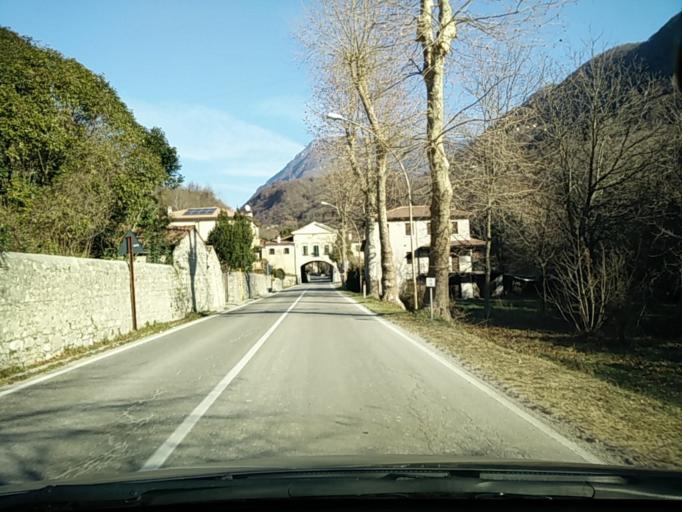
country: IT
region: Veneto
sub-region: Provincia di Treviso
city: Revine
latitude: 46.0099
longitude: 12.2874
